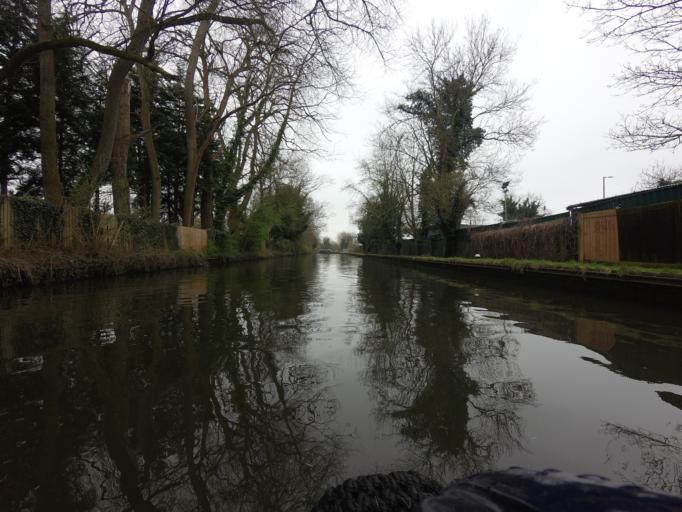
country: GB
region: England
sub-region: Hertfordshire
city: Abbots Langley
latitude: 51.6900
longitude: -0.4346
